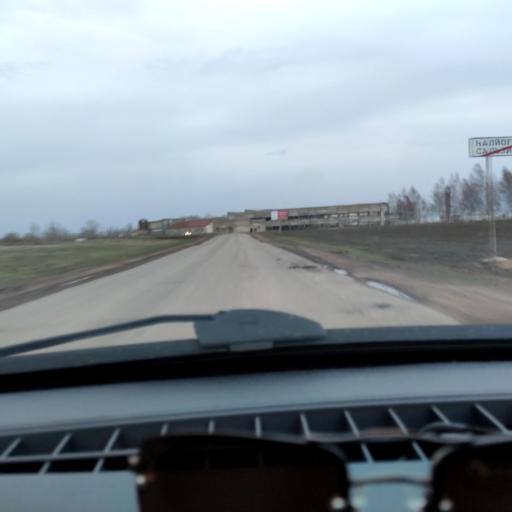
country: RU
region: Bashkortostan
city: Kabakovo
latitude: 54.5487
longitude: 56.1072
